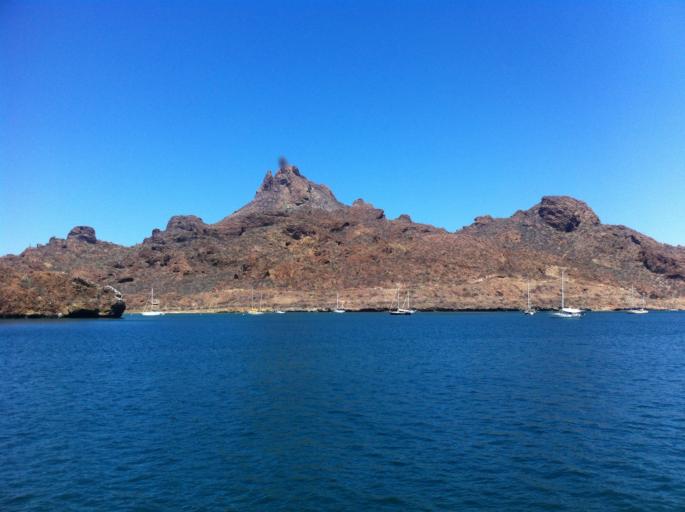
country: MX
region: Sonora
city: Heroica Guaymas
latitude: 27.9416
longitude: -111.0594
